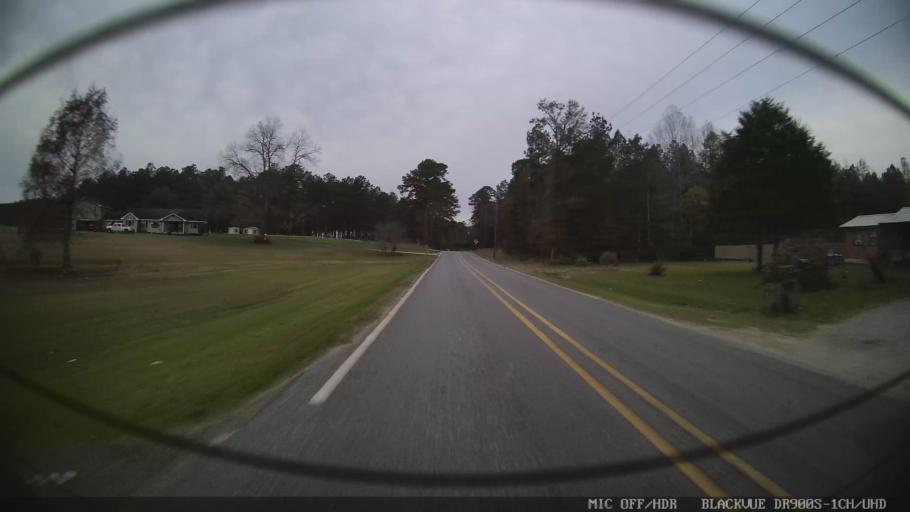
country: US
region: Mississippi
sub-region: Clarke County
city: Quitman
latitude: 32.0288
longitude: -88.8145
